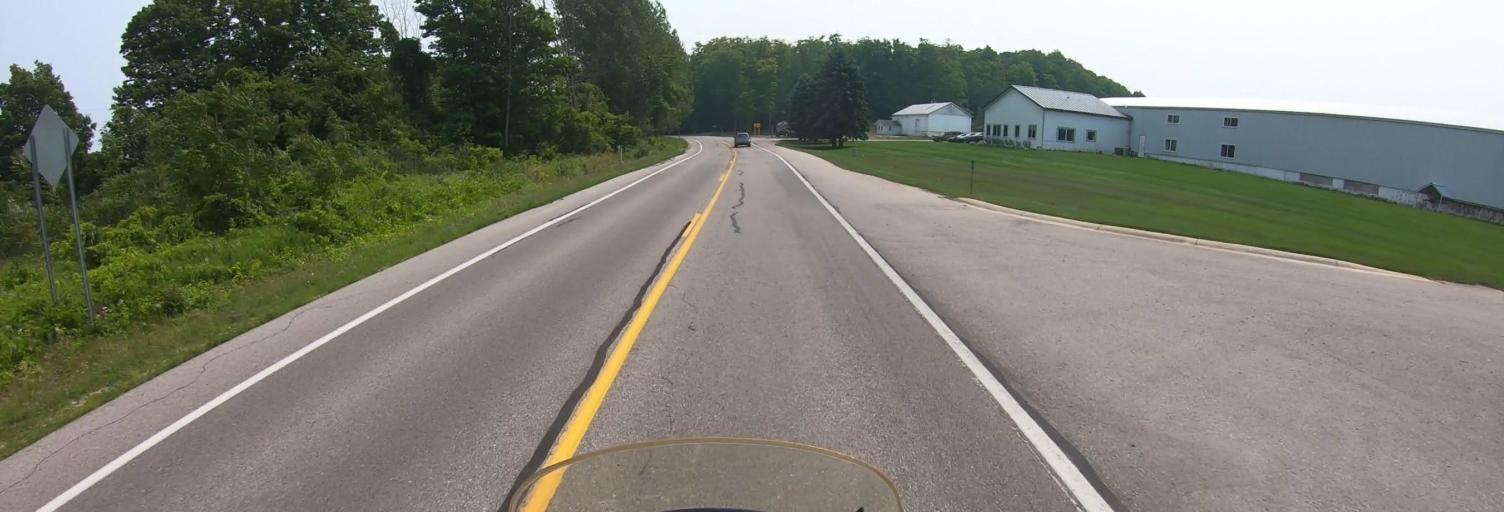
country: US
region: Michigan
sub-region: Leelanau County
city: Leland
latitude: 45.0872
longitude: -85.5996
